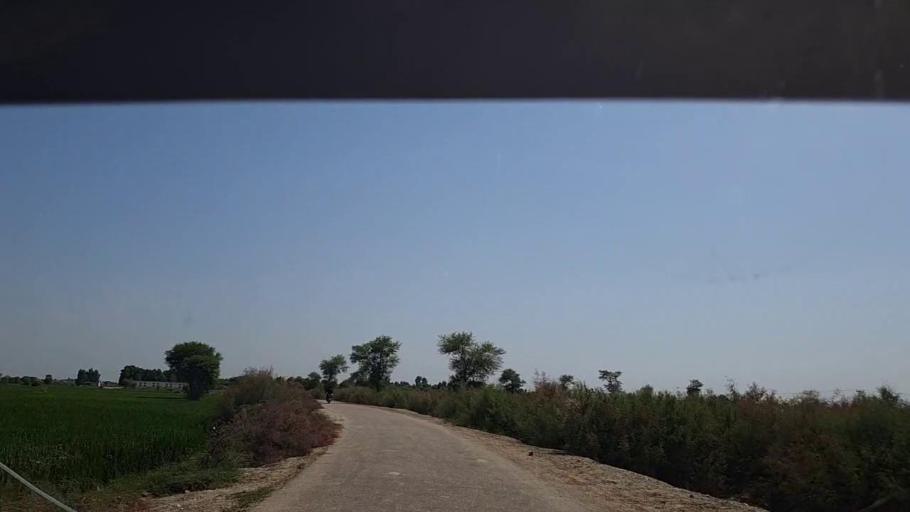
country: PK
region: Sindh
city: Kandhkot
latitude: 28.1678
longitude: 69.1604
